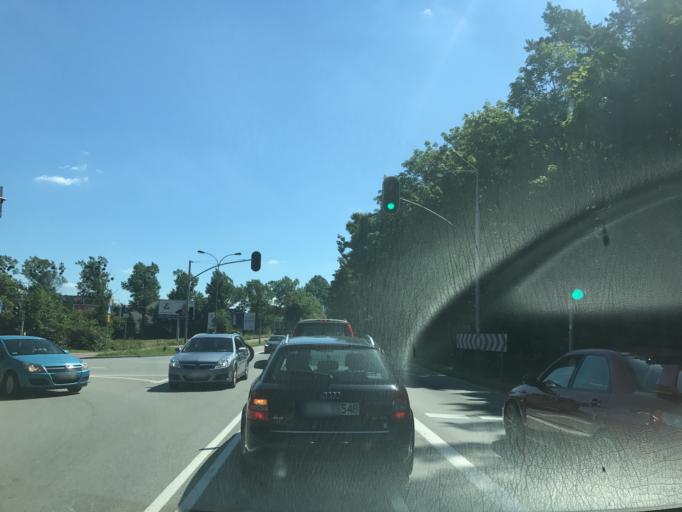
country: PL
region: Pomeranian Voivodeship
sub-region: Powiat gdanski
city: Lublewo Gdanskie
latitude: 54.3542
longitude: 18.4893
